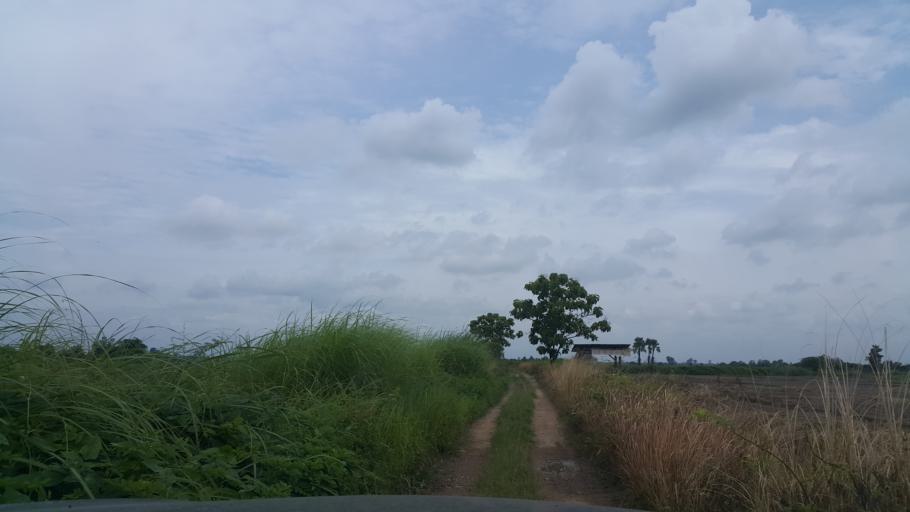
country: TH
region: Lamphun
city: Ban Thi
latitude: 18.6372
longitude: 99.1542
